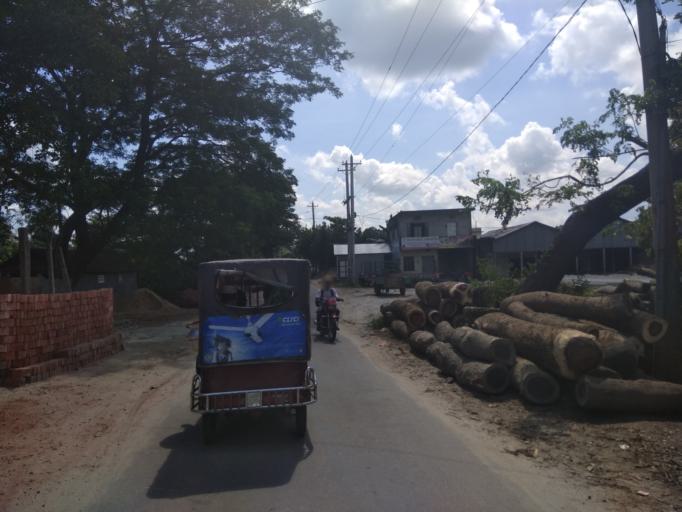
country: BD
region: Dhaka
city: Narayanganj
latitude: 23.5029
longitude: 90.4655
